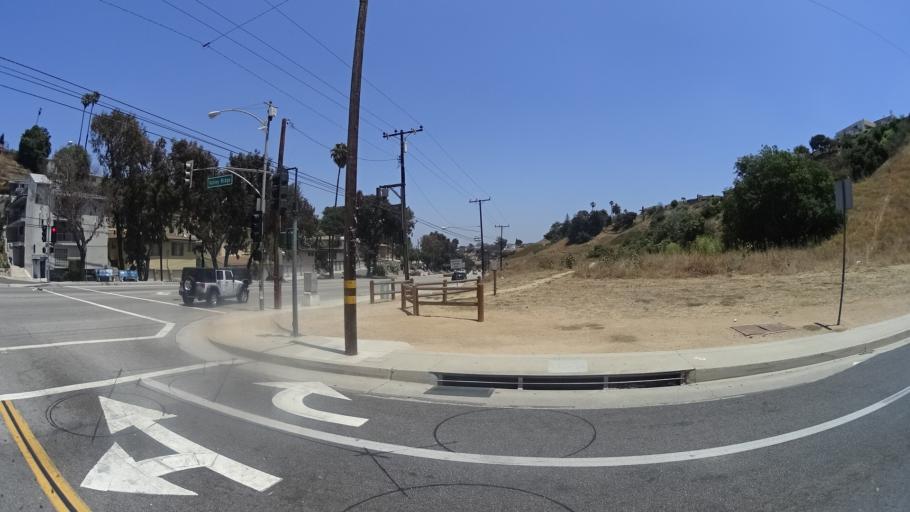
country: US
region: California
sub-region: Los Angeles County
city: View Park-Windsor Hills
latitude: 34.0045
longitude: -118.3474
